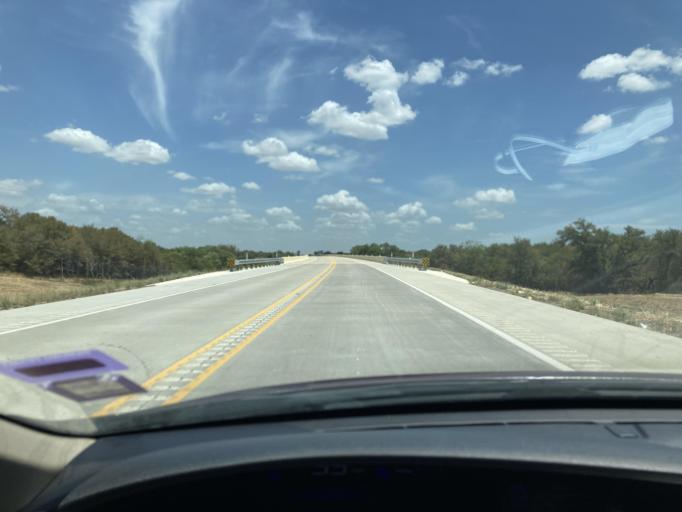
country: US
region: Texas
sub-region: Navarro County
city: Corsicana
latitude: 32.0534
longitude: -96.4136
